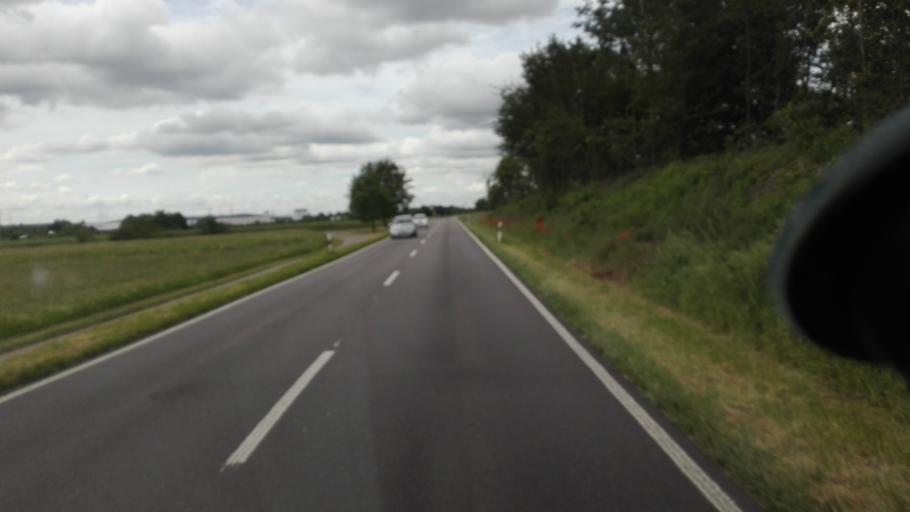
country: DE
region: Baden-Wuerttemberg
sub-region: Karlsruhe Region
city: Ubstadt-Weiher
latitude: 49.1772
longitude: 8.6285
